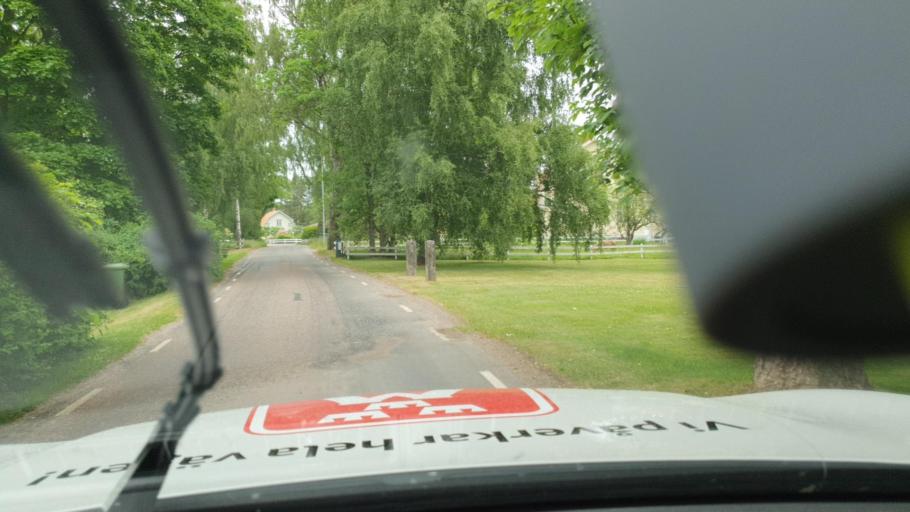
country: SE
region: Vaestra Goetaland
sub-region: Hjo Kommun
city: Hjo
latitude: 58.3092
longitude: 14.2507
